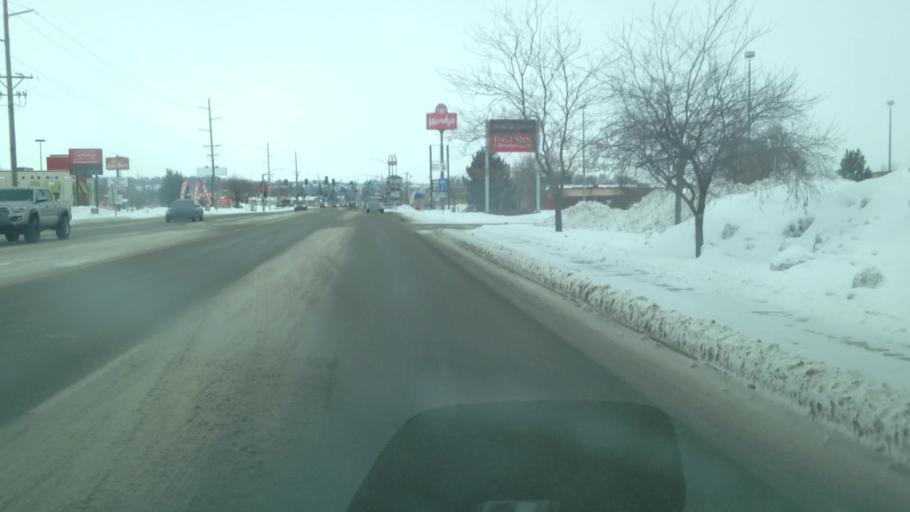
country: US
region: Idaho
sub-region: Madison County
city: Rexburg
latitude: 43.8392
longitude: -111.7782
